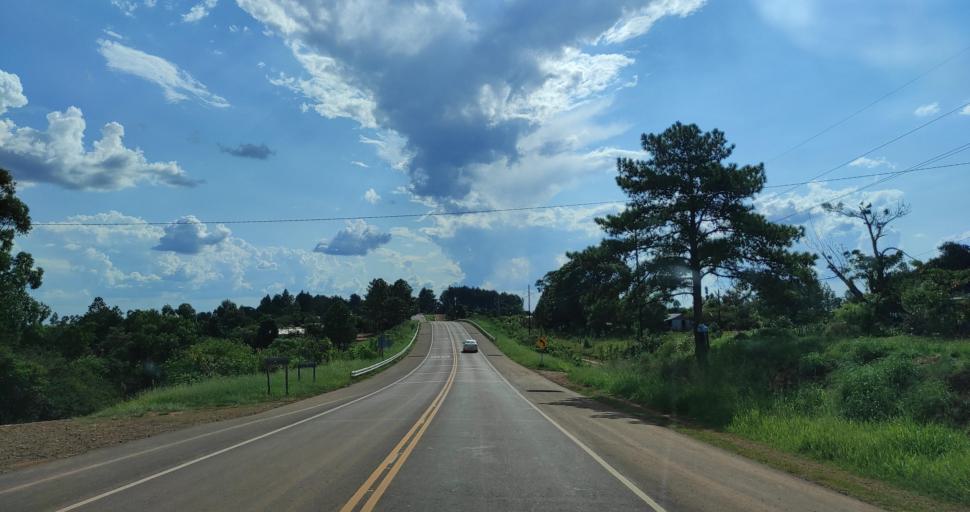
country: AR
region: Misiones
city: Bernardo de Irigoyen
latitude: -26.2958
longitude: -53.7904
